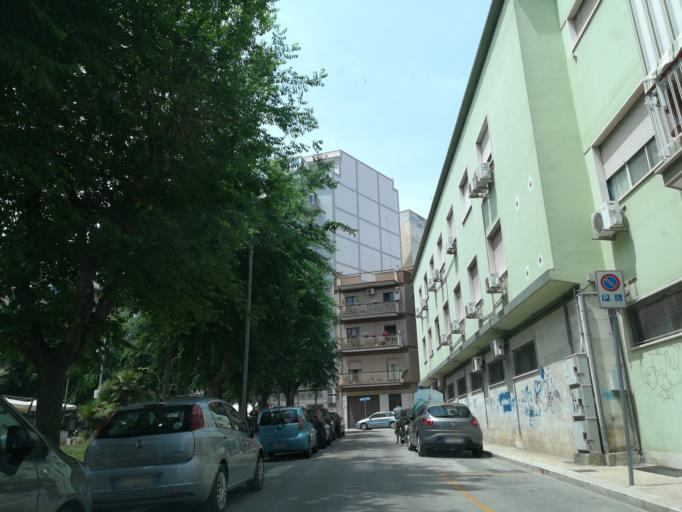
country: IT
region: Apulia
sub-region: Provincia di Barletta - Andria - Trani
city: Barletta
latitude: 41.3186
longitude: 16.2839
